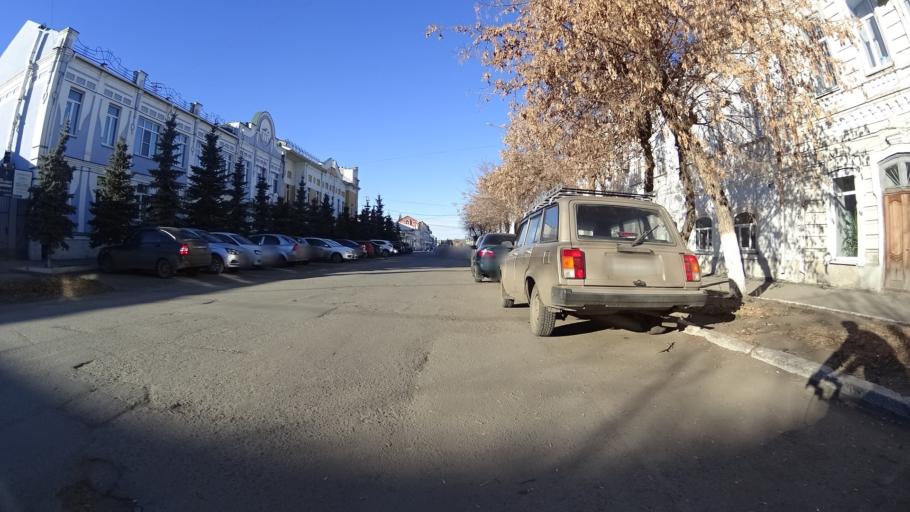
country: RU
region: Chelyabinsk
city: Troitsk
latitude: 54.0847
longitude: 61.5587
